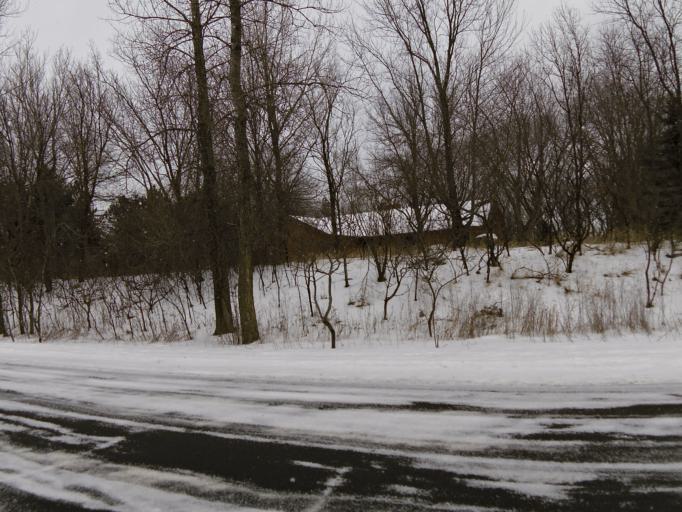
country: US
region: Minnesota
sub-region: Washington County
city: Lake Elmo
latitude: 44.9723
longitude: -92.8418
